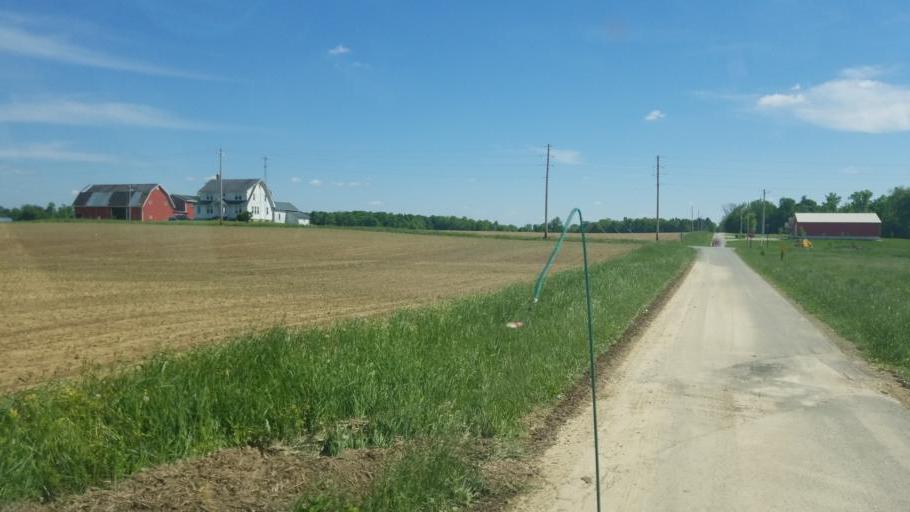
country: US
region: Ohio
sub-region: Crawford County
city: Bucyrus
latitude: 40.9367
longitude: -83.0357
